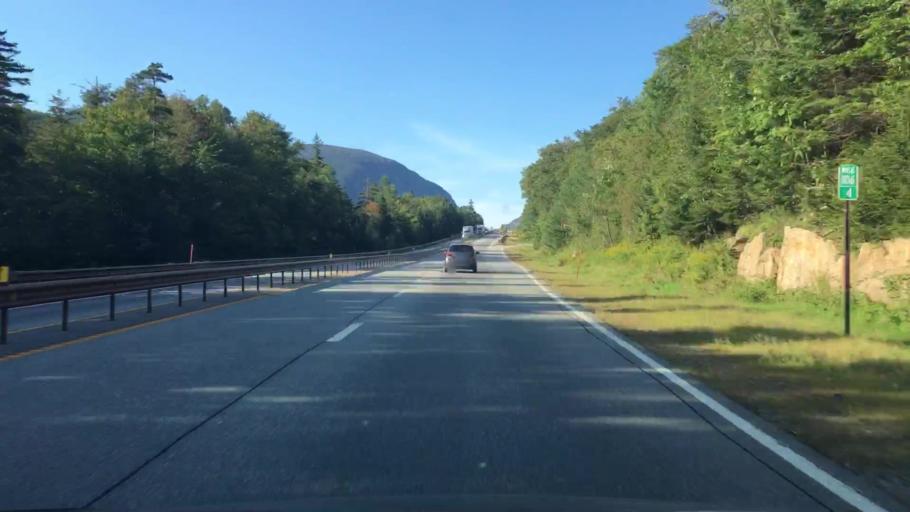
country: US
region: New Hampshire
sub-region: Grafton County
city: Deerfield
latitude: 44.1174
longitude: -71.6821
